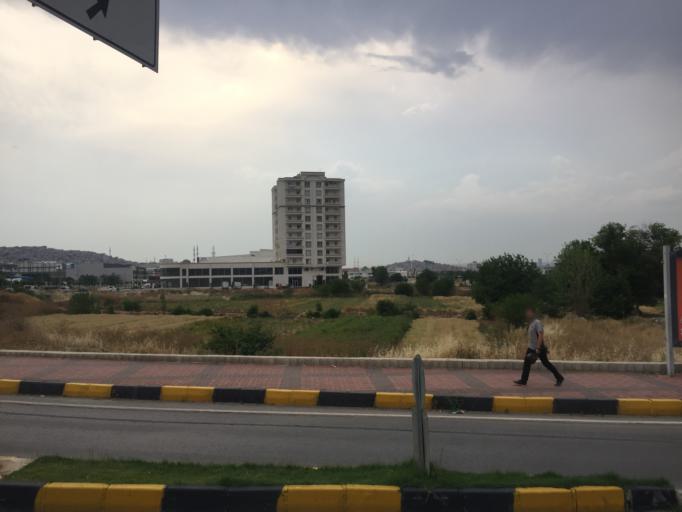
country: TR
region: Gaziantep
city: Gaziantep
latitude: 37.0558
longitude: 37.4156
